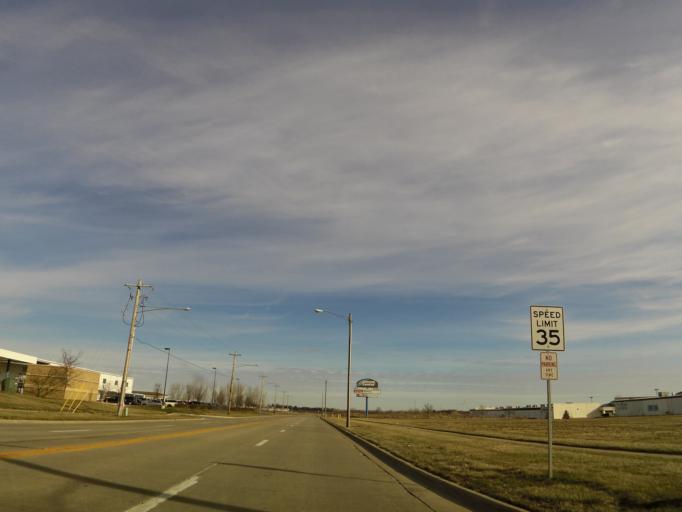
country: US
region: Illinois
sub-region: McLean County
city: Bloomington
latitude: 40.4942
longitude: -89.0354
